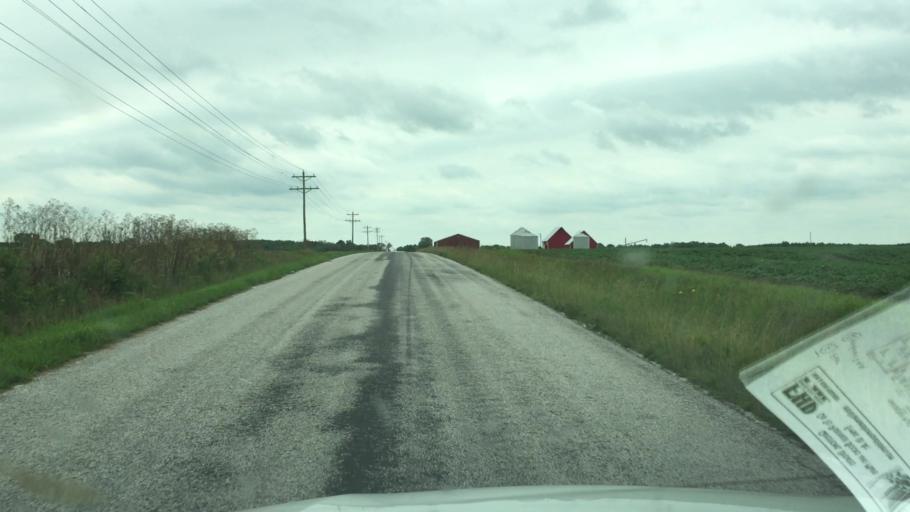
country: US
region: Illinois
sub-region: Hancock County
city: Carthage
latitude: 40.2935
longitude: -91.0833
